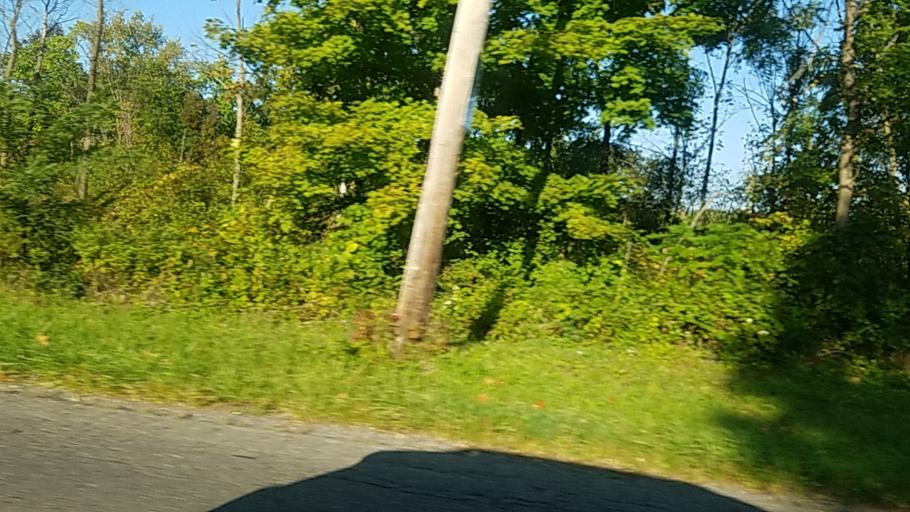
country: US
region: Ohio
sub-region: Trumbull County
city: Niles
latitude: 41.1682
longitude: -80.7534
